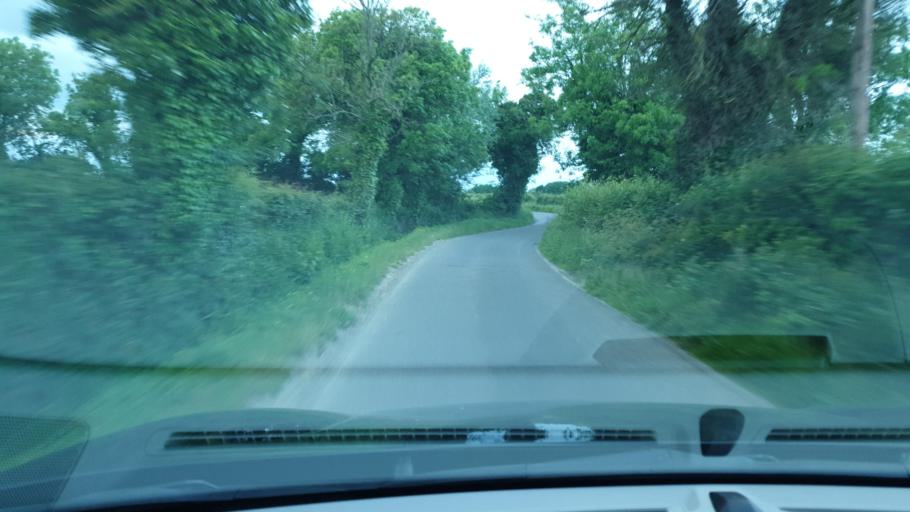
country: IE
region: Leinster
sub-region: An Mhi
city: Ashbourne
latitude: 53.5185
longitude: -6.3855
